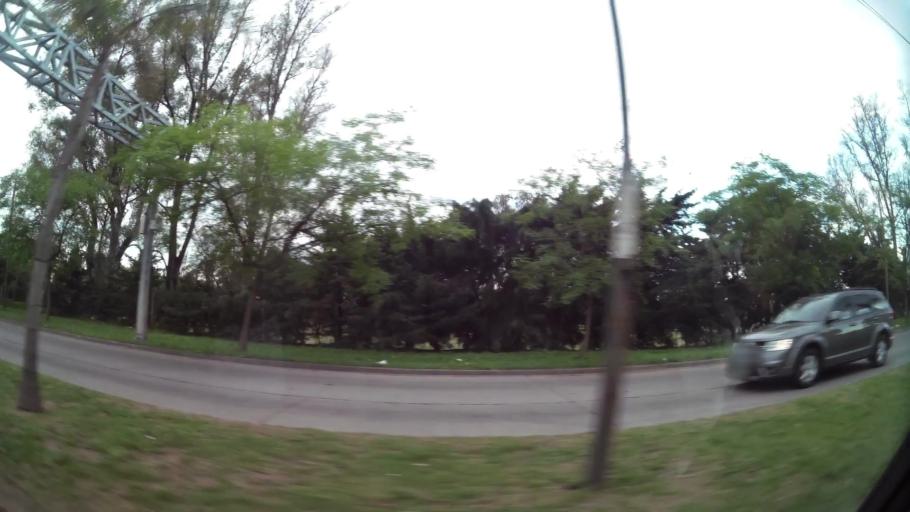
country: AR
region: Buenos Aires
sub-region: Partido de Tigre
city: Tigre
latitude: -34.4842
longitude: -58.5899
